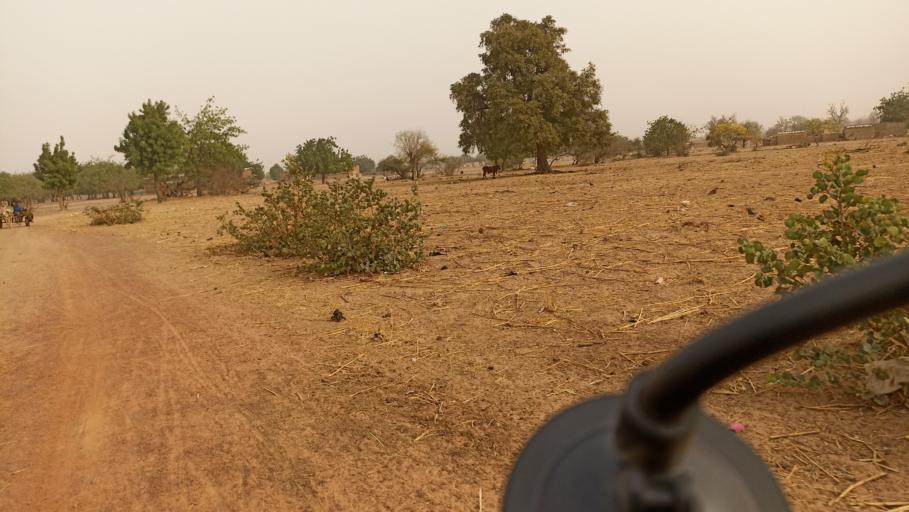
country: BF
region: Boucle du Mouhoun
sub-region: Province du Nayala
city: Toma
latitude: 12.8663
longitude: -2.7480
